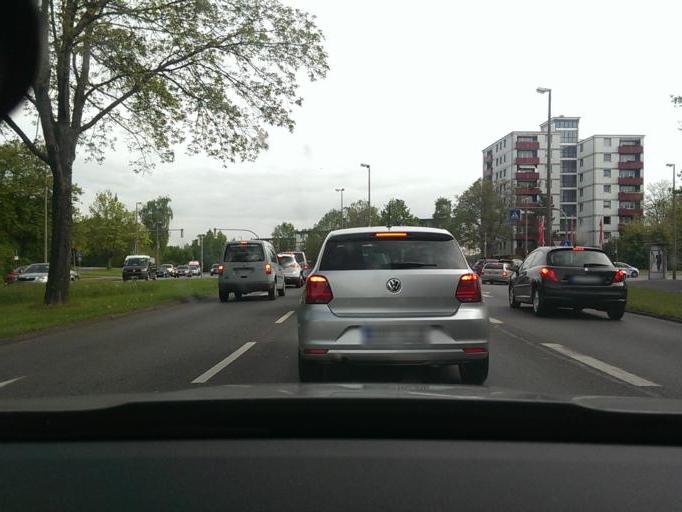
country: DE
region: Lower Saxony
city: Wolfsburg
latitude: 52.4187
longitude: 10.7994
